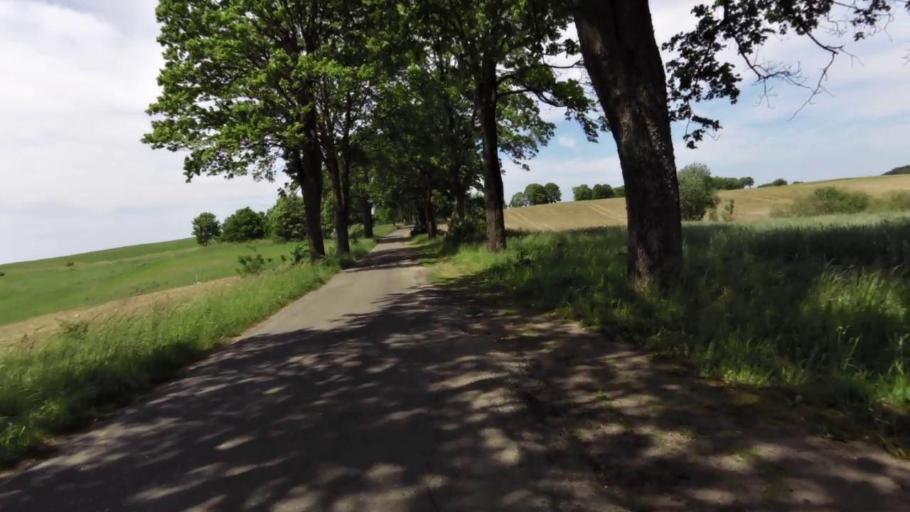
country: PL
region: West Pomeranian Voivodeship
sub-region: Powiat szczecinecki
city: Szczecinek
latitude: 53.6496
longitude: 16.6765
